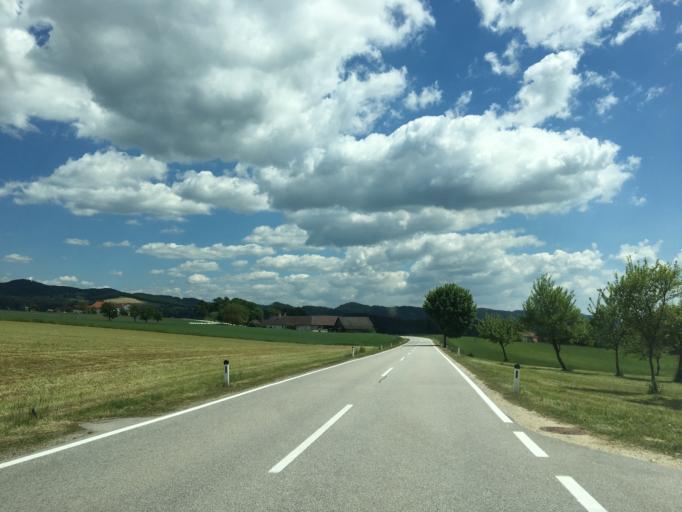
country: AT
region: Upper Austria
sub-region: Politischer Bezirk Freistadt
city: Freistadt
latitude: 48.4516
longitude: 14.5088
